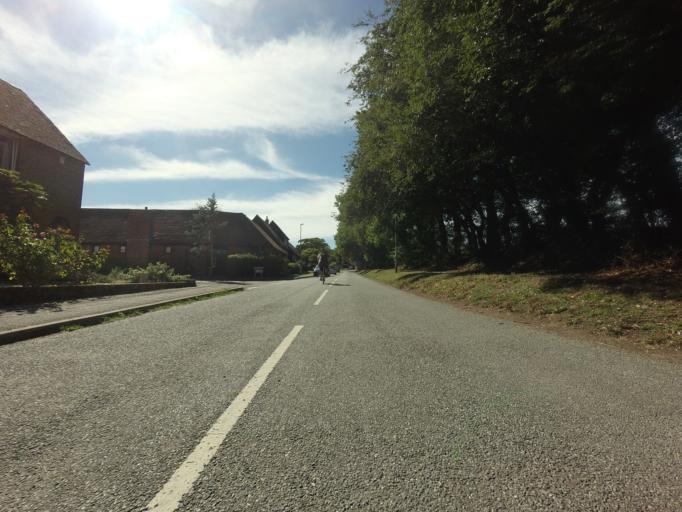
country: GB
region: England
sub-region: Kent
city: Birchington-on-Sea
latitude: 51.3406
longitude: 1.2731
